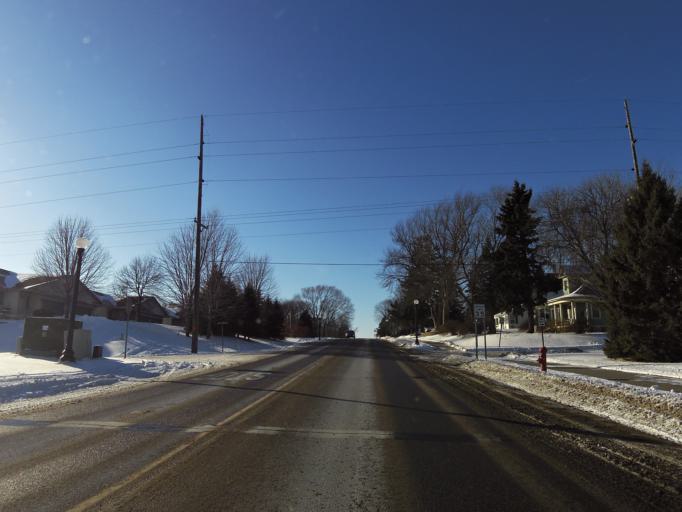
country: US
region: Minnesota
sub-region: Le Sueur County
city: New Prague
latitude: 44.5436
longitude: -93.5857
